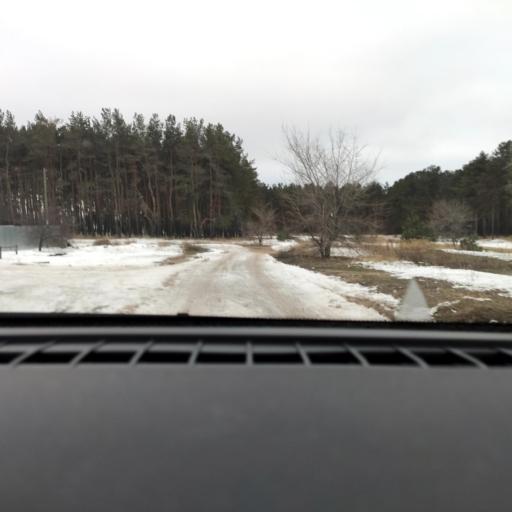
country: RU
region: Voronezj
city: Maslovka
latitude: 51.6058
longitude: 39.2162
